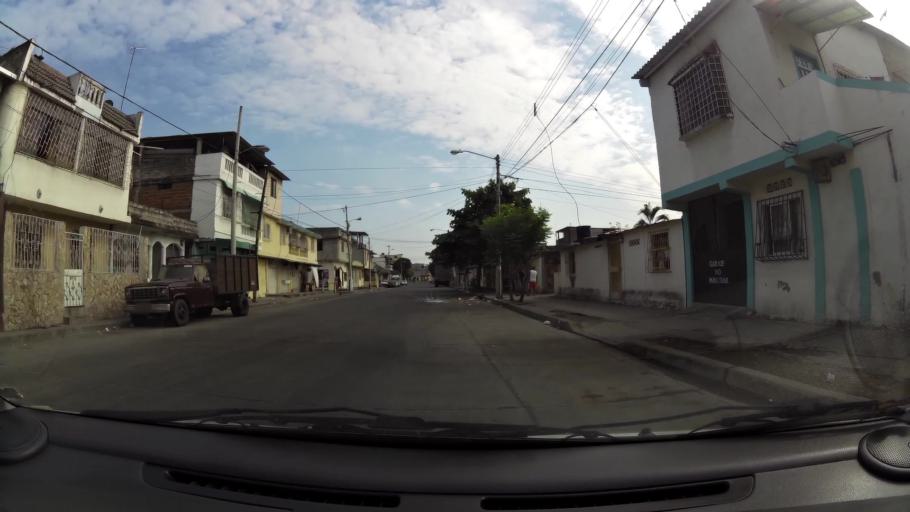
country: EC
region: Guayas
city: Guayaquil
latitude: -2.2456
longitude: -79.8882
